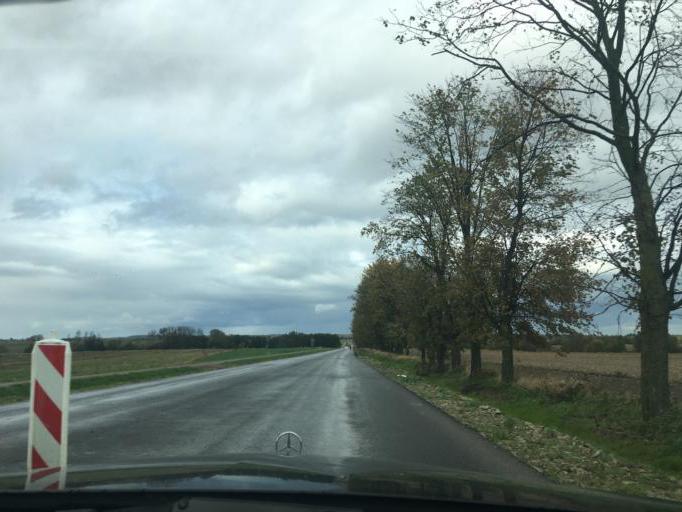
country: PL
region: Lublin Voivodeship
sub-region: Powiat lubelski
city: Wysokie
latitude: 50.9334
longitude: 22.6722
